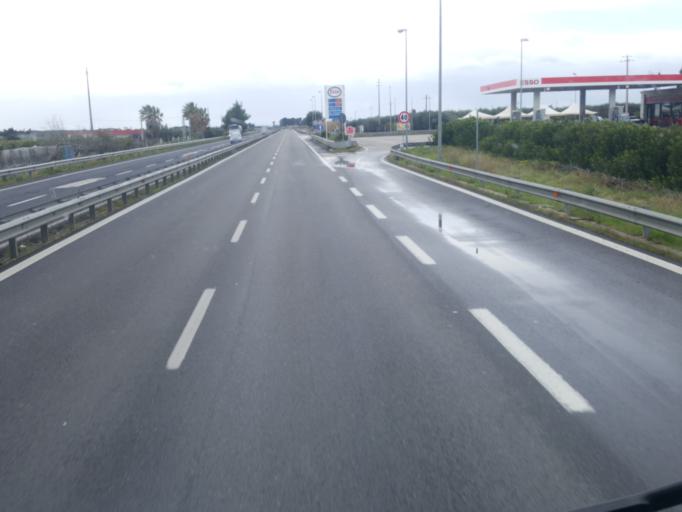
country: IT
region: Apulia
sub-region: Provincia di Taranto
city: Palagiano
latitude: 40.5275
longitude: 17.0494
